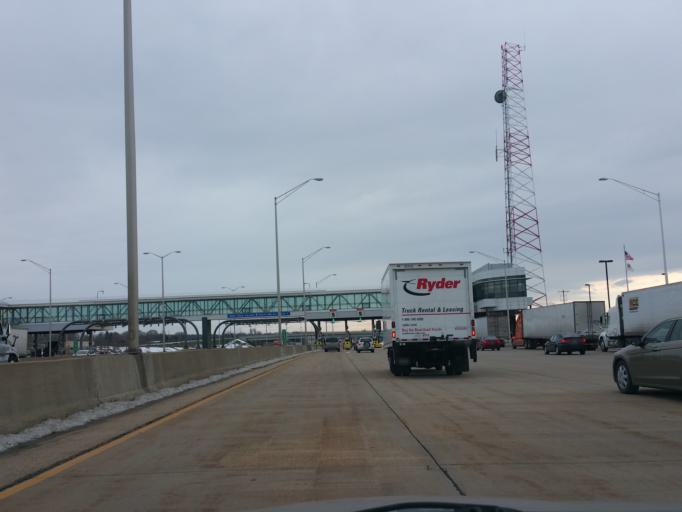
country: US
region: Illinois
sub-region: Winnebago County
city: Roscoe
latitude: 42.4463
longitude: -88.9932
